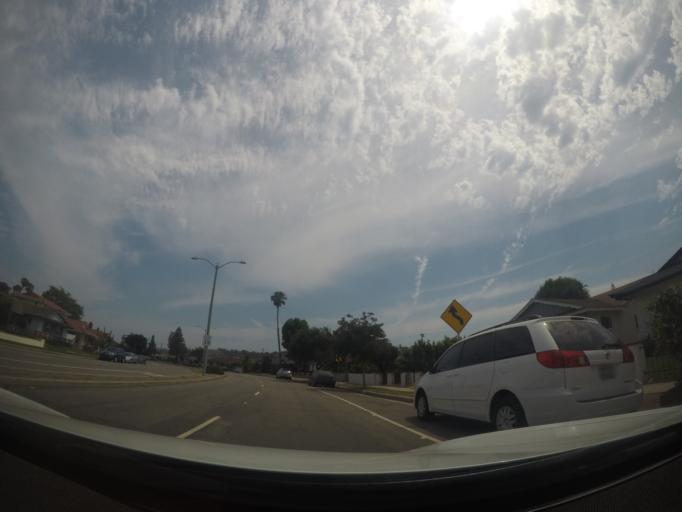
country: US
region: California
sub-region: Los Angeles County
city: Torrance
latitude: 33.8168
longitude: -118.3600
